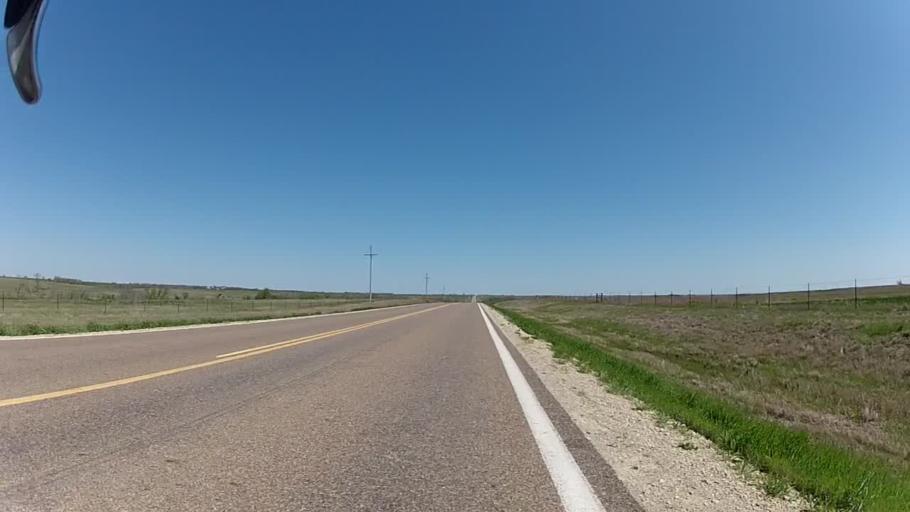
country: US
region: Kansas
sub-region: Morris County
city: Council Grove
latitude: 38.9008
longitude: -96.5202
